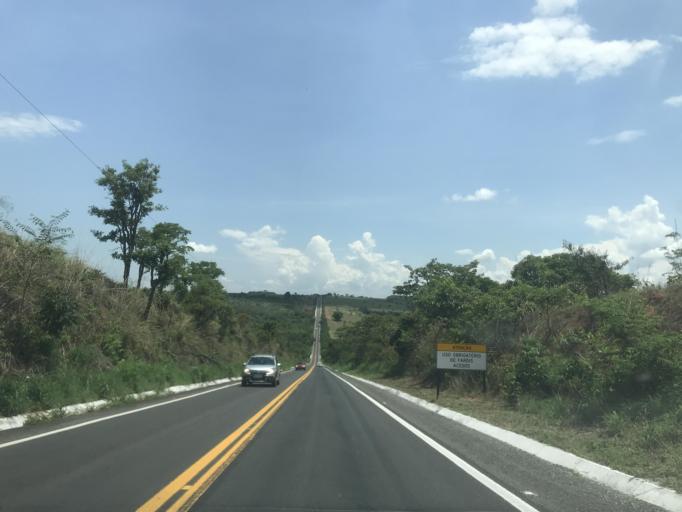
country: BR
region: Goias
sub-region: Bela Vista De Goias
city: Bela Vista de Goias
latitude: -17.1176
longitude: -48.6672
